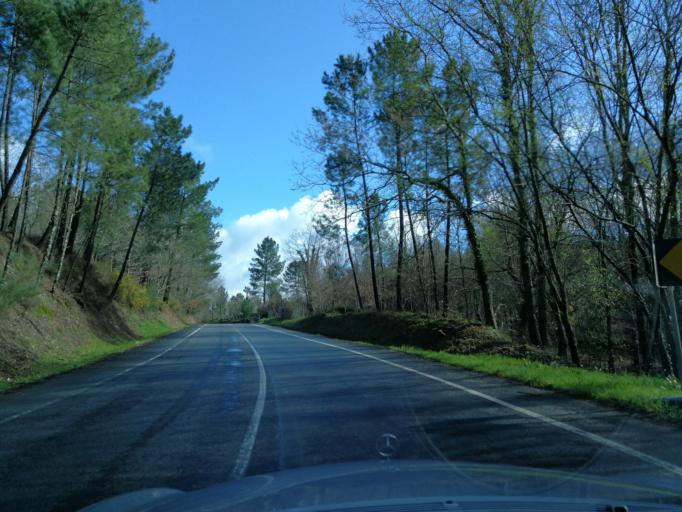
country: PT
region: Viana do Castelo
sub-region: Ponte da Barca
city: Ponte da Barca
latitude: 41.8098
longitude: -8.3426
